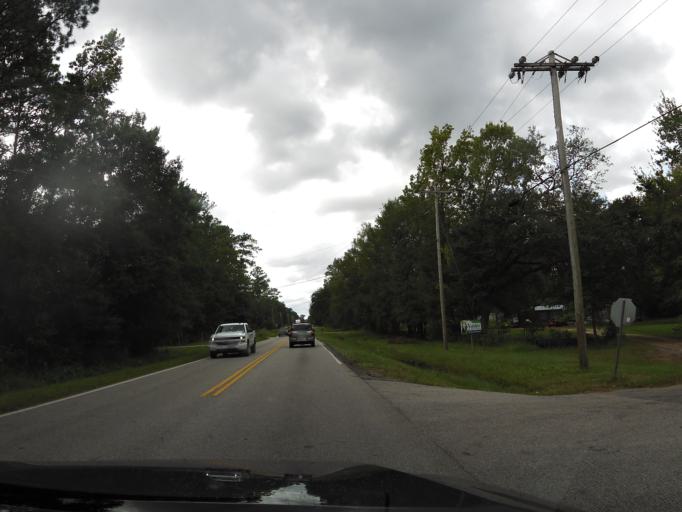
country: US
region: Florida
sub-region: Clay County
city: Lakeside
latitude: 30.1046
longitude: -81.8034
